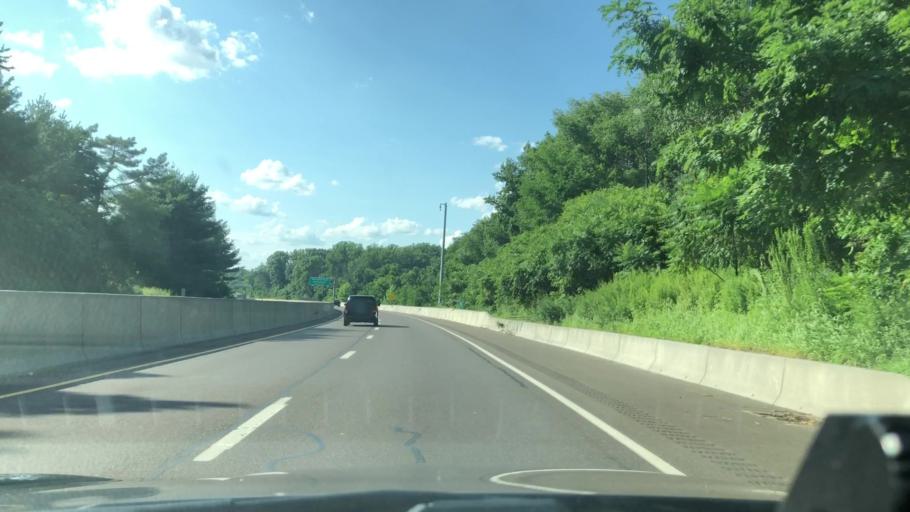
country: US
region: Pennsylvania
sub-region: Montgomery County
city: Ambler
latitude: 40.1643
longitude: -75.2021
